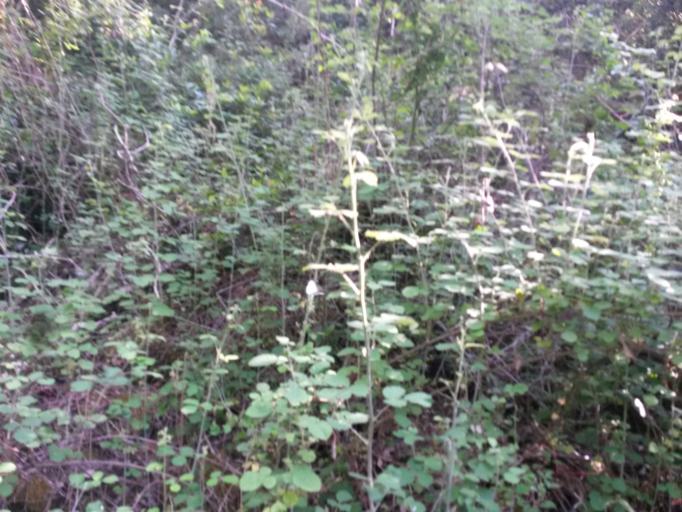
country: GR
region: North Aegean
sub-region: Nomos Lesvou
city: Agiasos
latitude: 39.1127
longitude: 26.3910
